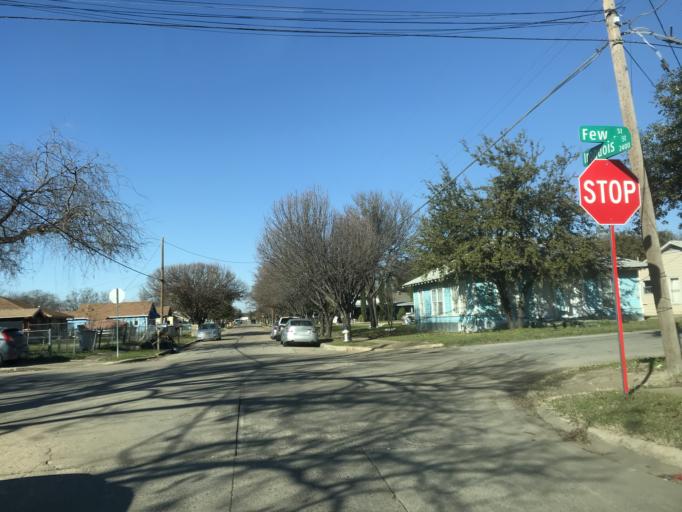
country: US
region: Texas
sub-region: Dallas County
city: Cockrell Hill
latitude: 32.7728
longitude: -96.9063
